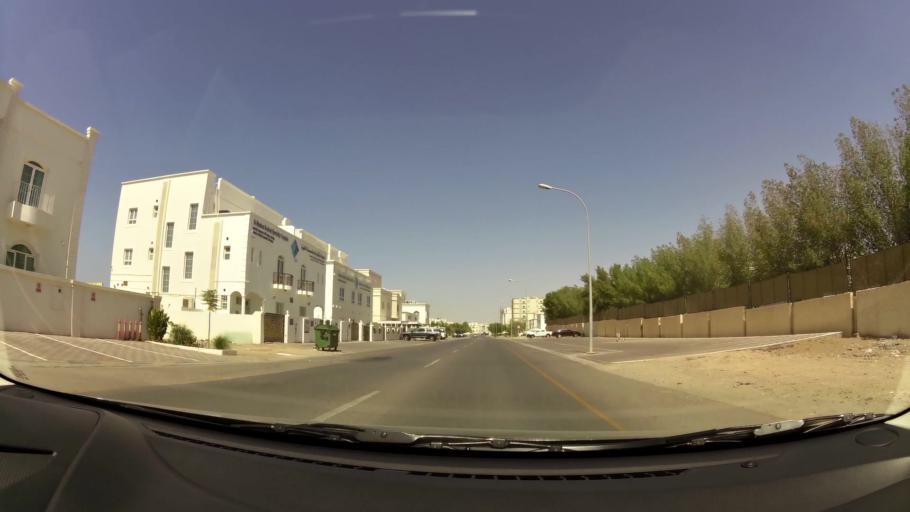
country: OM
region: Muhafazat Masqat
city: Bawshar
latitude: 23.5971
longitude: 58.3561
